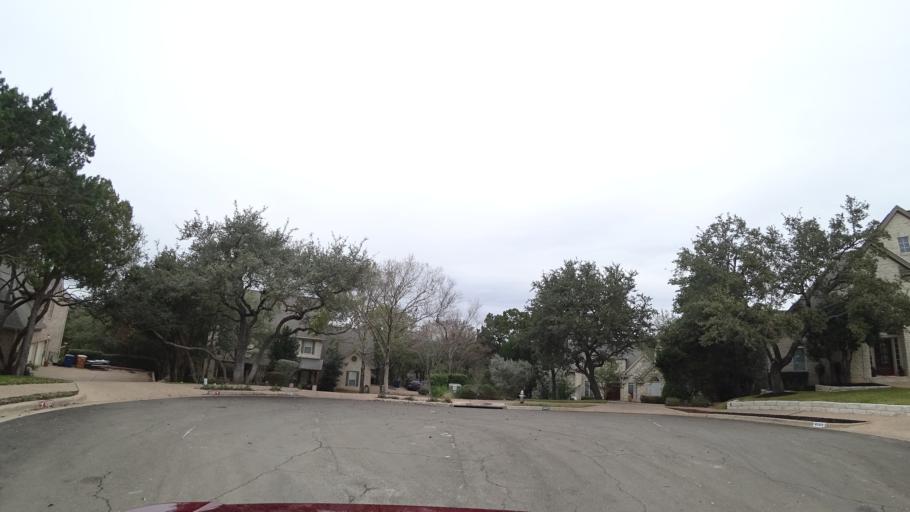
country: US
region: Texas
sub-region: Williamson County
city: Jollyville
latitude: 30.3930
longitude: -97.8056
